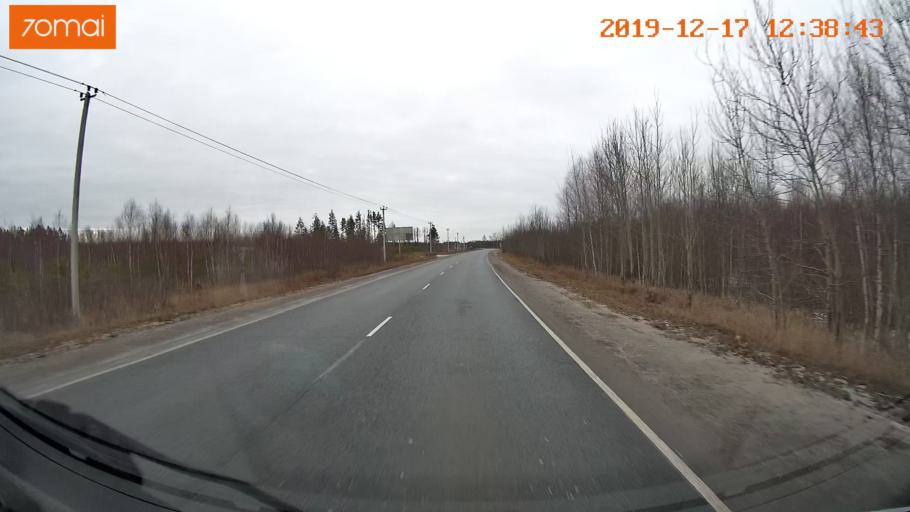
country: RU
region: Moskovskaya
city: Radovitskiy
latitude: 54.9760
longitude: 39.9513
